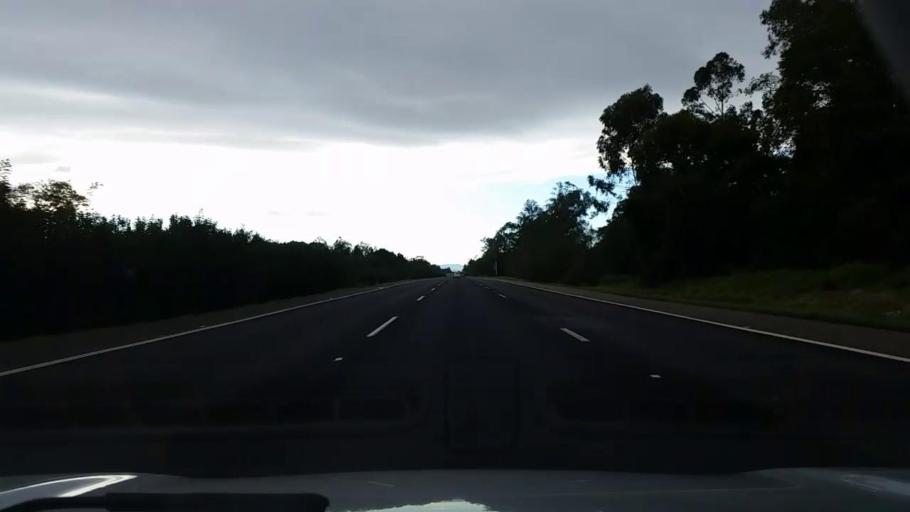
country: BR
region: Rio Grande do Sul
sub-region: Taquara
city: Taquara
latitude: -29.8903
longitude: -50.7041
